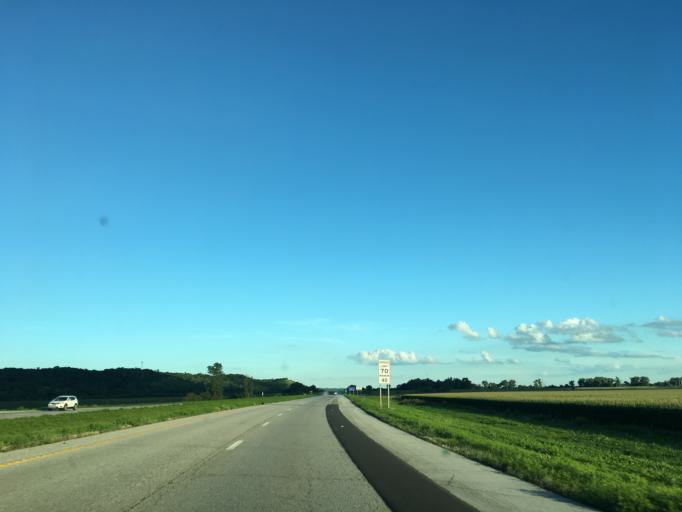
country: US
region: Iowa
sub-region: Fremont County
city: Hamburg
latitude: 40.5829
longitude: -95.6510
